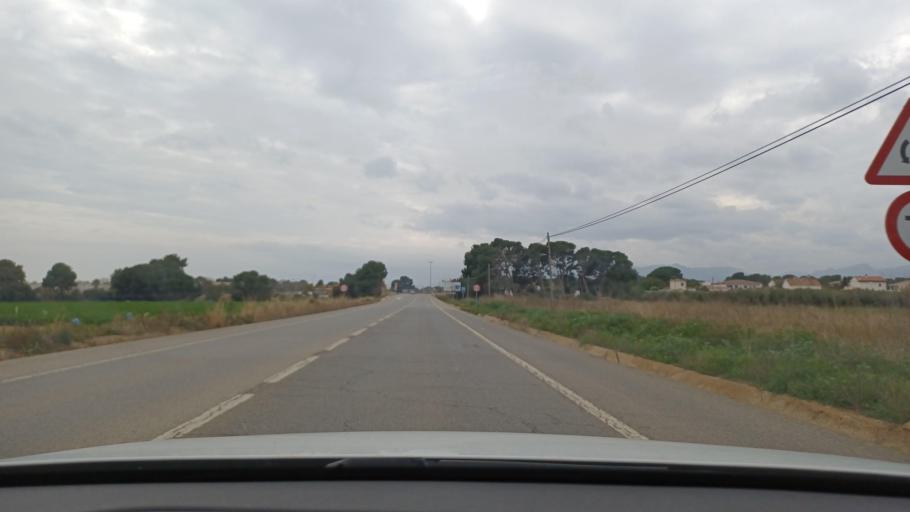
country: ES
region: Catalonia
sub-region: Provincia de Tarragona
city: Cambrils
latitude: 41.0522
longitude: 1.0031
